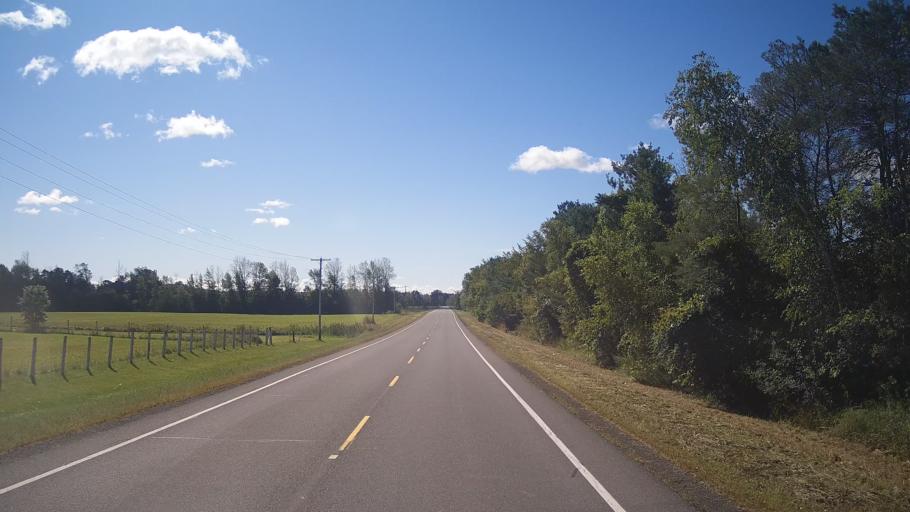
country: CA
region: Ontario
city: Prescott
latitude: 44.9117
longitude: -75.4071
